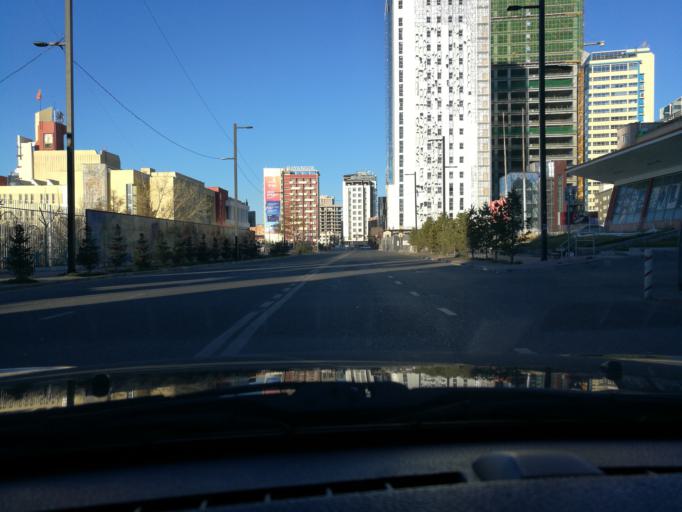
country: MN
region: Ulaanbaatar
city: Ulaanbaatar
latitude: 47.9135
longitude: 106.9178
